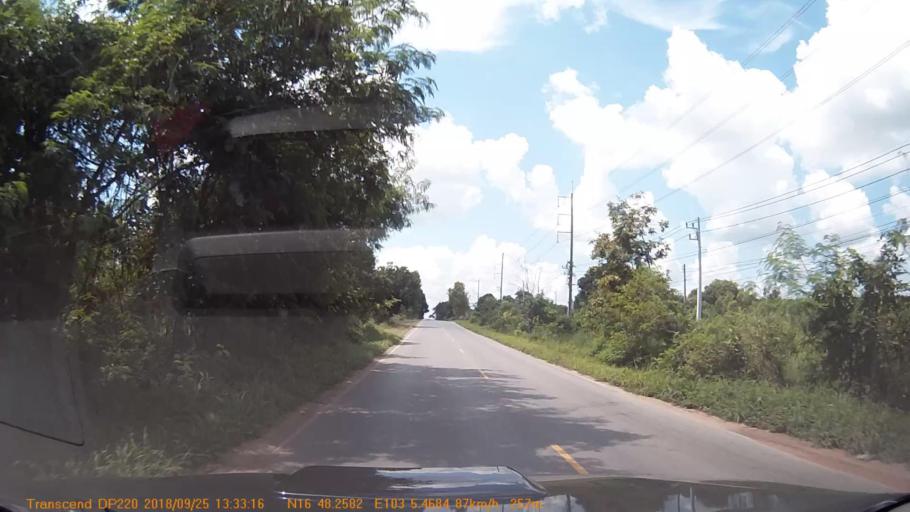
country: TH
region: Khon Kaen
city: Kranuan
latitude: 16.8043
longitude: 103.0911
